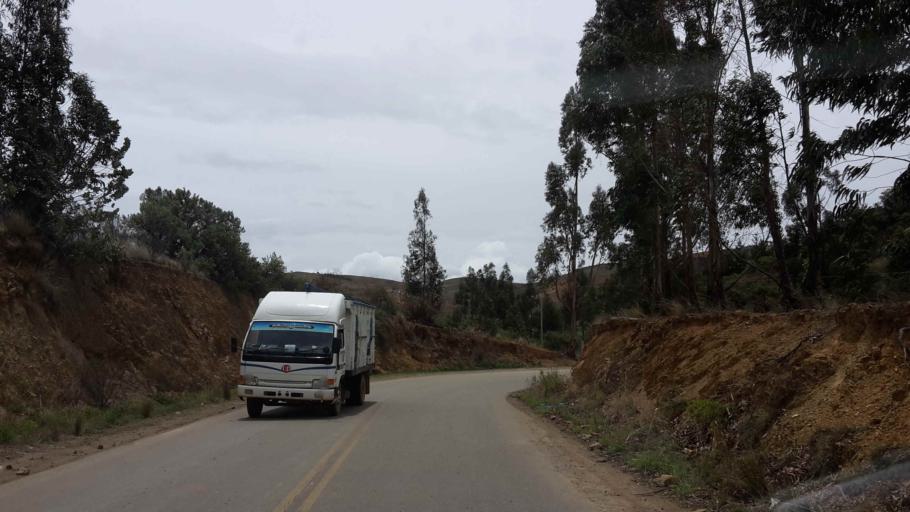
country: BO
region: Cochabamba
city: Totora
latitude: -17.7038
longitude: -65.2133
